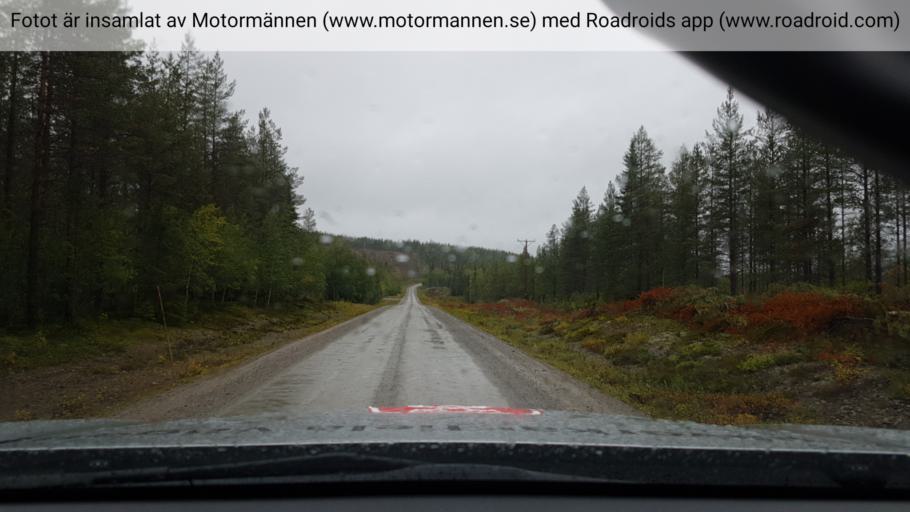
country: SE
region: Vaesterbotten
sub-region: Asele Kommun
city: Insjon
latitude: 64.0868
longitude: 17.8905
